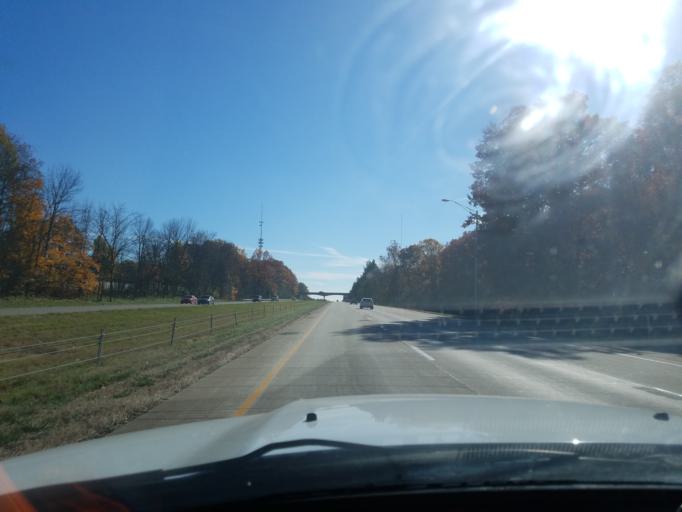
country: US
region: Indiana
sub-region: Bartholomew County
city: Columbus
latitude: 39.1914
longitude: -85.9591
